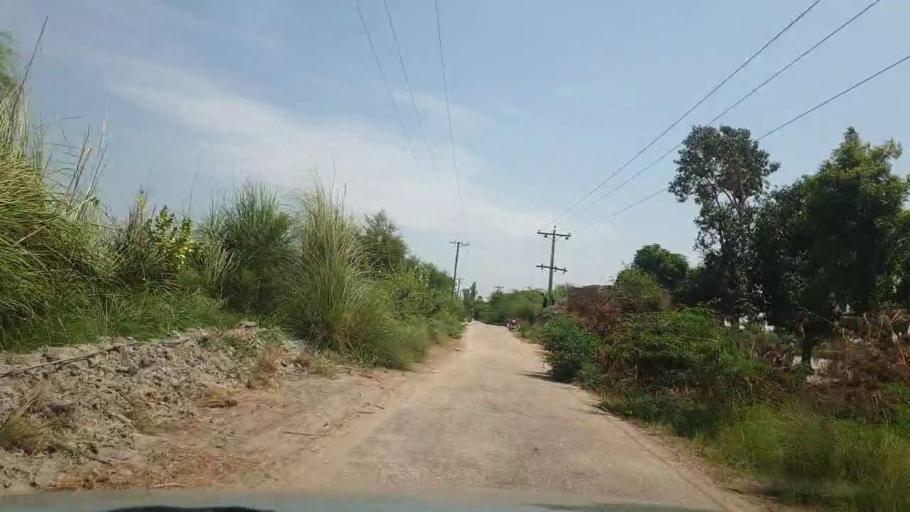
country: PK
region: Sindh
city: Kot Diji
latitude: 27.1226
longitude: 68.9956
